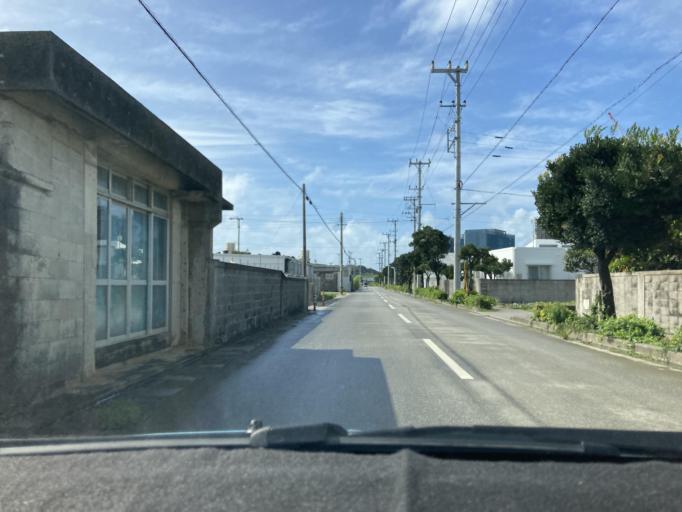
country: JP
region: Okinawa
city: Itoman
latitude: 26.1036
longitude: 127.6624
